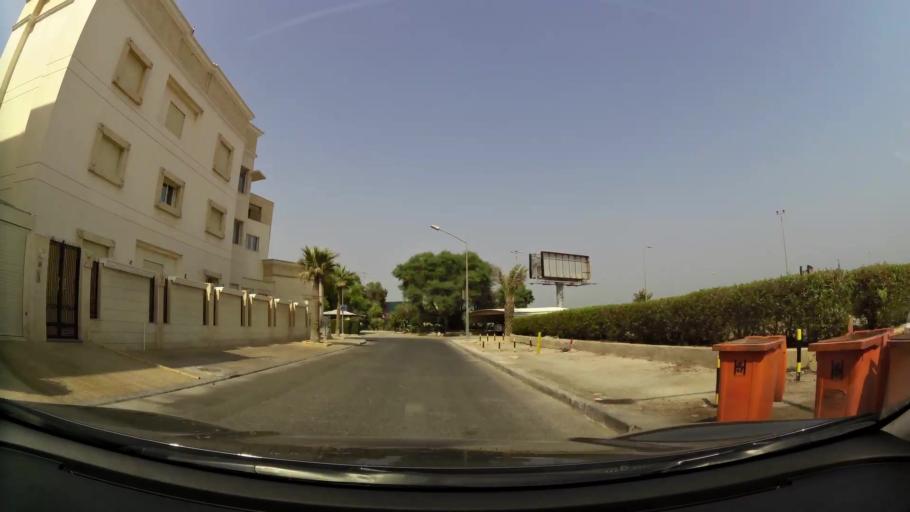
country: KW
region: Al Asimah
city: Ad Dasmah
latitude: 29.3595
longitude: 48.0182
